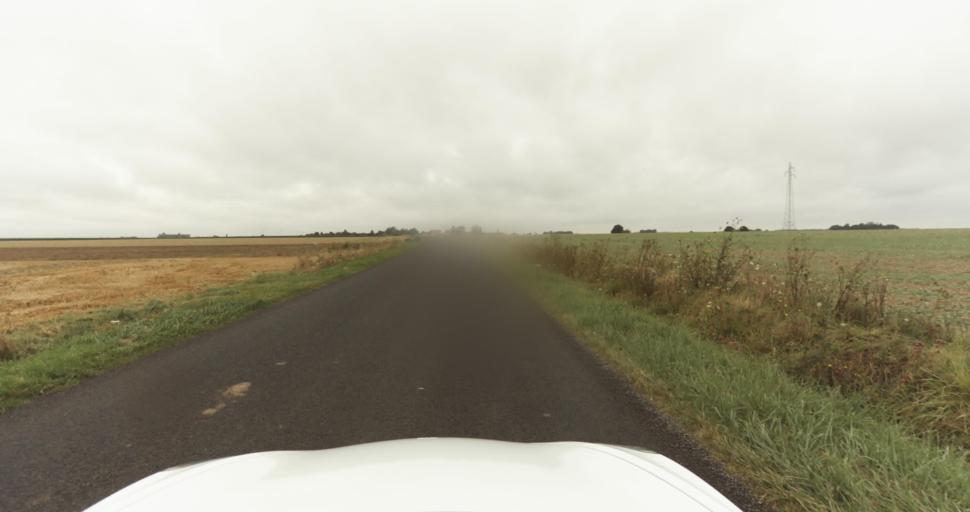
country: FR
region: Haute-Normandie
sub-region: Departement de l'Eure
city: Claville
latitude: 49.0887
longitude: 1.0617
